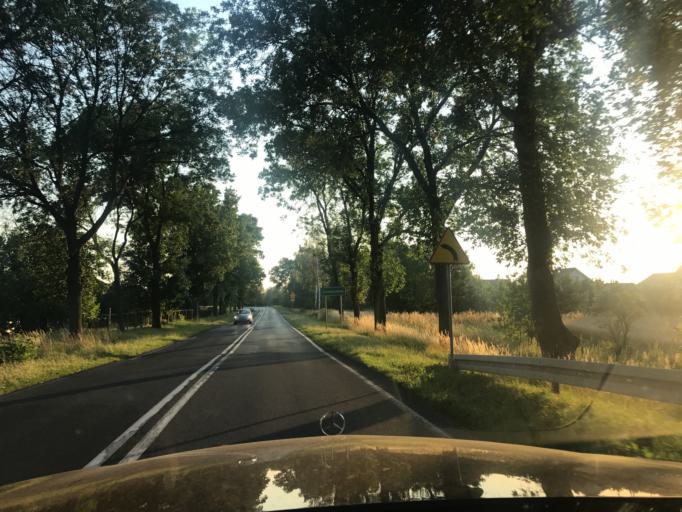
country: PL
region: Lublin Voivodeship
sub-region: Powiat lubartowski
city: Lubartow
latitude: 51.4979
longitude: 22.6427
